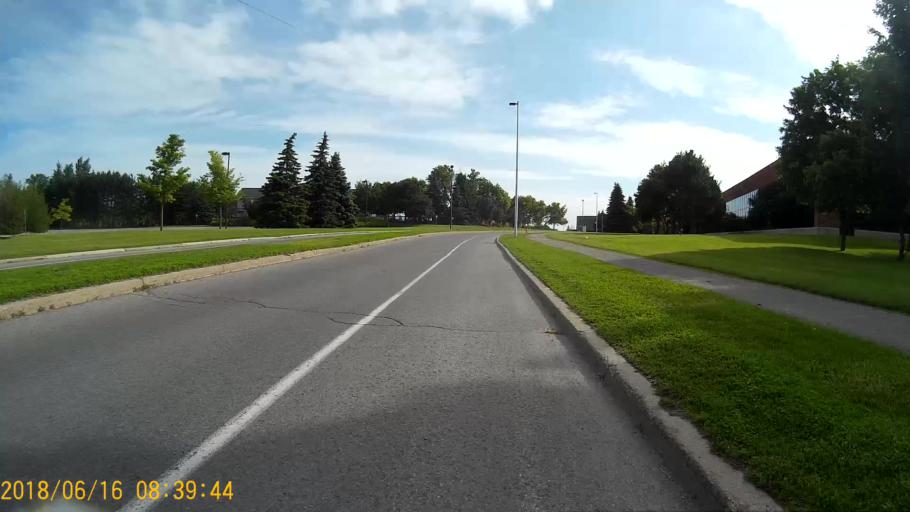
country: CA
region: Ontario
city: Bells Corners
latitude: 45.3512
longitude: -75.9178
